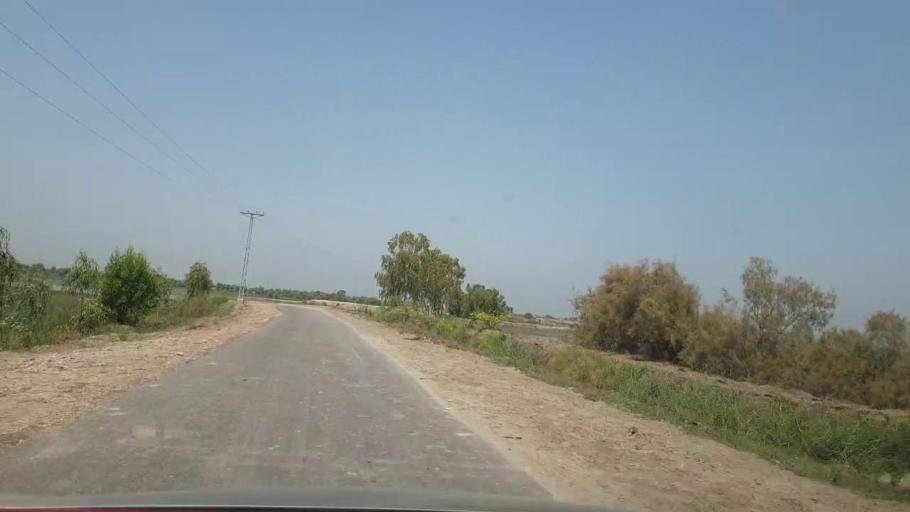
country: PK
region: Sindh
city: Warah
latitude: 27.4752
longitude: 67.7589
